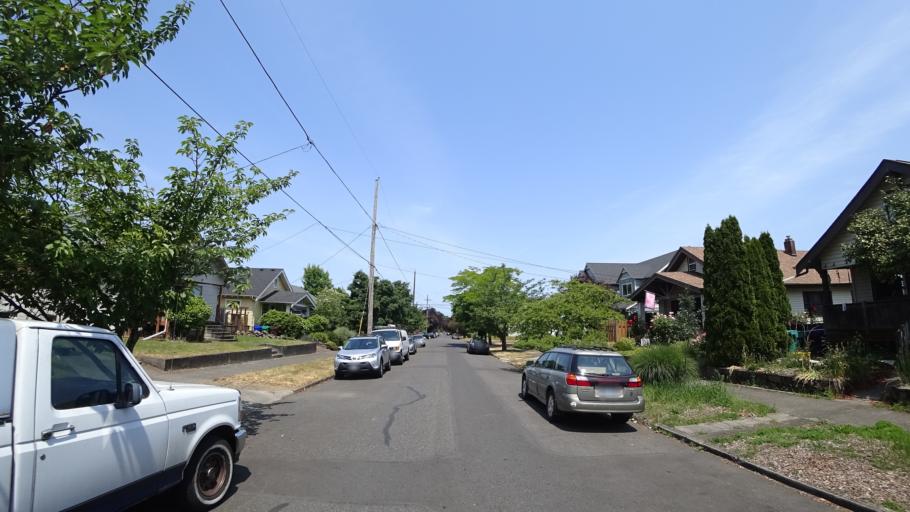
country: US
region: Oregon
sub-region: Multnomah County
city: Portland
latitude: 45.5782
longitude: -122.6891
